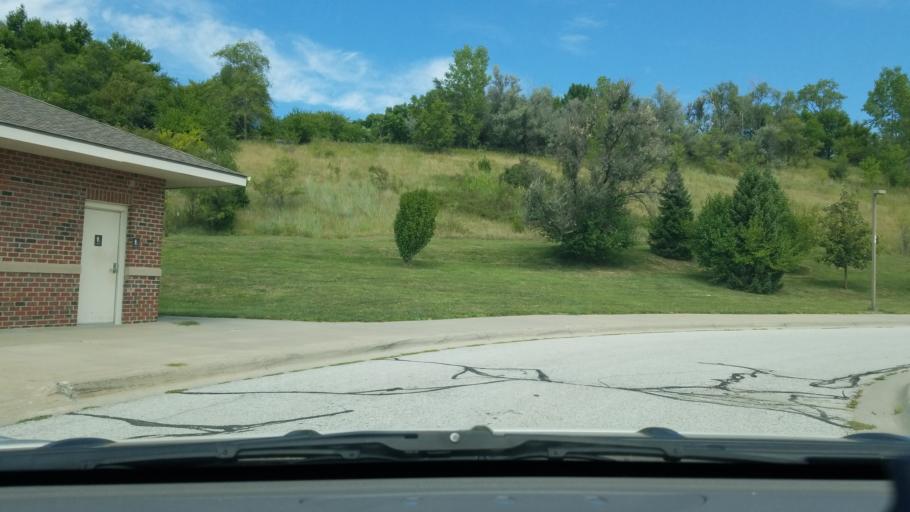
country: US
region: Nebraska
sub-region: Sarpy County
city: Offutt Air Force Base
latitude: 41.1429
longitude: -95.9305
